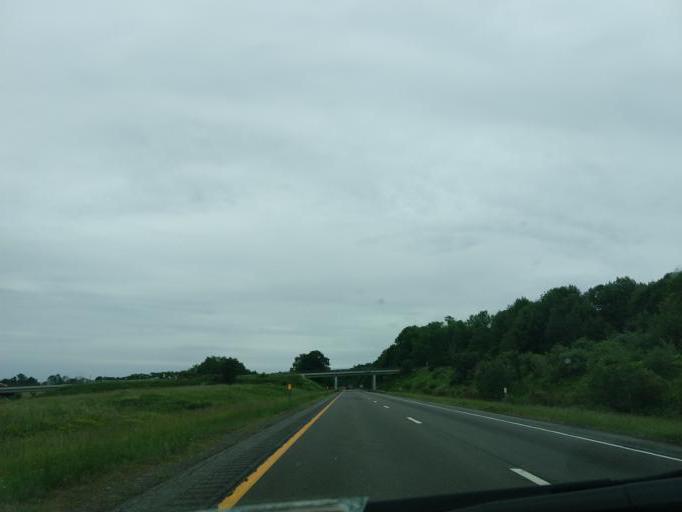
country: US
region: New York
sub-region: Broome County
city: Chenango Bridge
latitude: 42.2884
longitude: -75.9253
